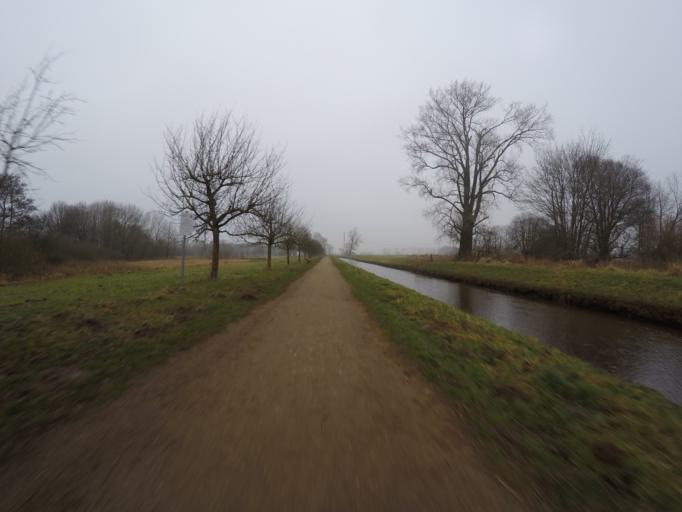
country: DE
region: Schleswig-Holstein
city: Borstel-Hohenraden
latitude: 53.6735
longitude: 9.8192
